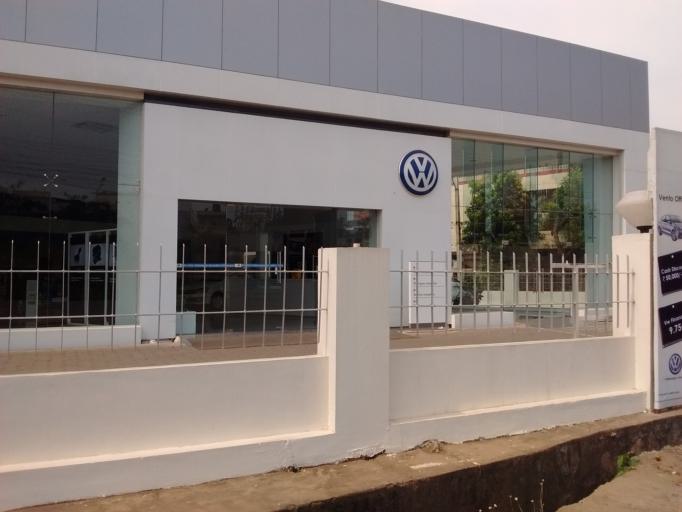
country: IN
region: Andhra Pradesh
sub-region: Krishna
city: Yanamalakuduru
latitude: 16.5235
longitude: 80.6768
